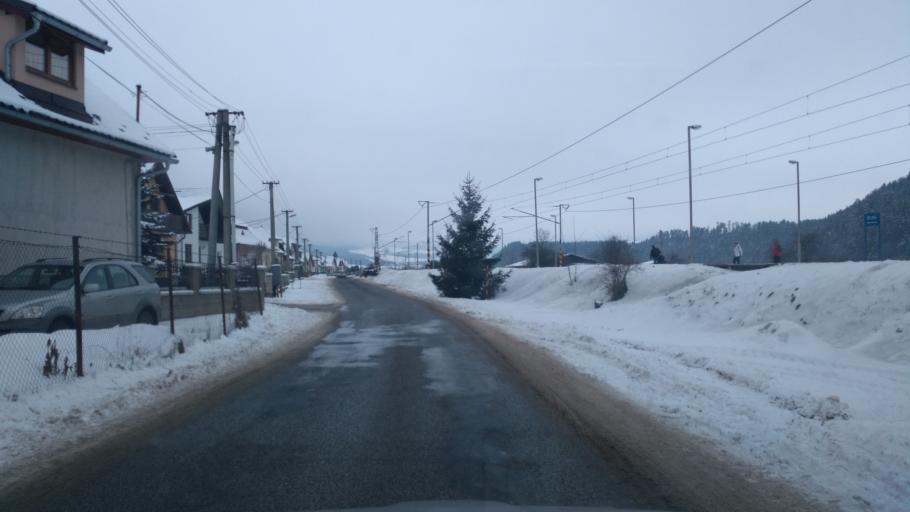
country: SK
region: Kosicky
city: Spisska Nova Ves
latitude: 48.9168
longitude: 20.6689
